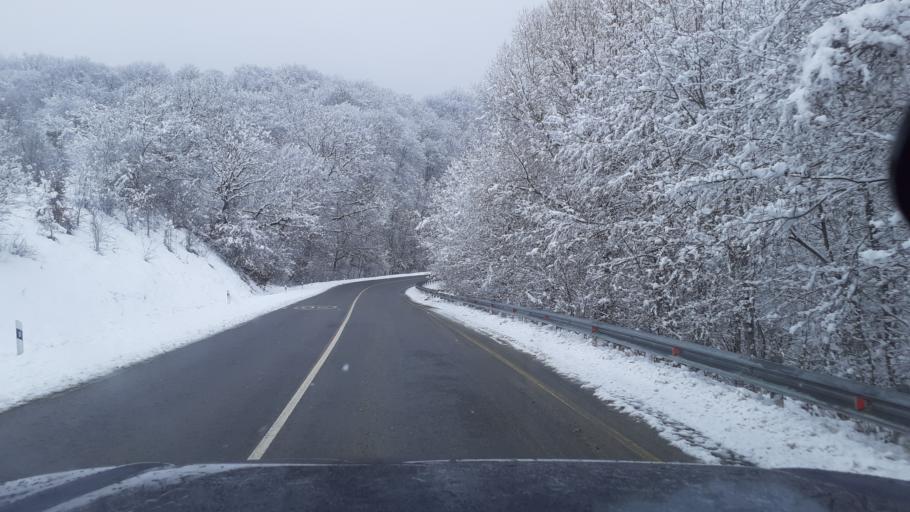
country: RU
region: Adygeya
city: Kamennomostskiy
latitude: 44.2129
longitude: 40.1818
